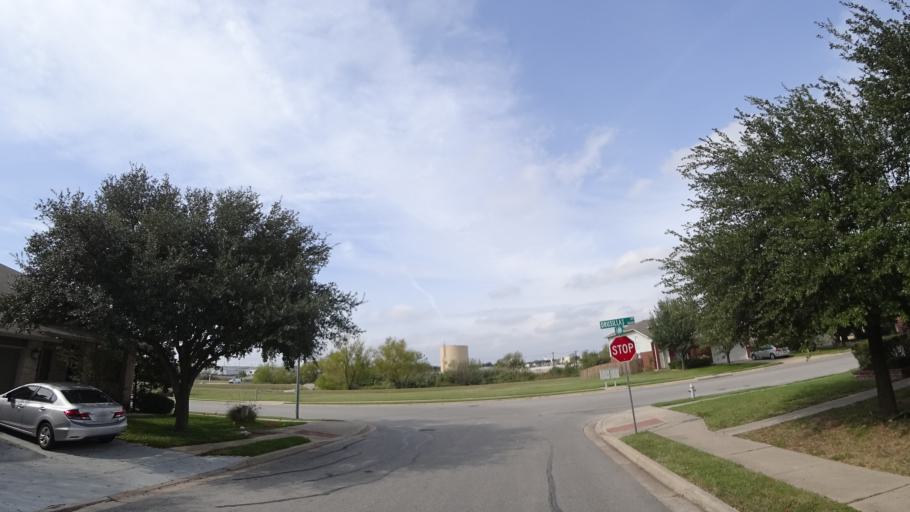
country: US
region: Texas
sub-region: Travis County
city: Windemere
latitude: 30.4390
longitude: -97.6583
